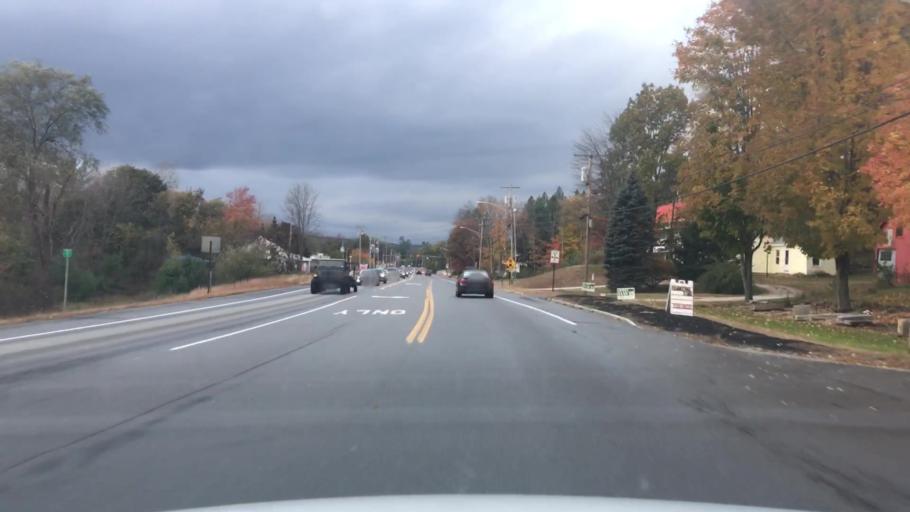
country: US
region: New Hampshire
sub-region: Merrimack County
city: Epsom
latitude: 43.2243
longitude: -71.3420
